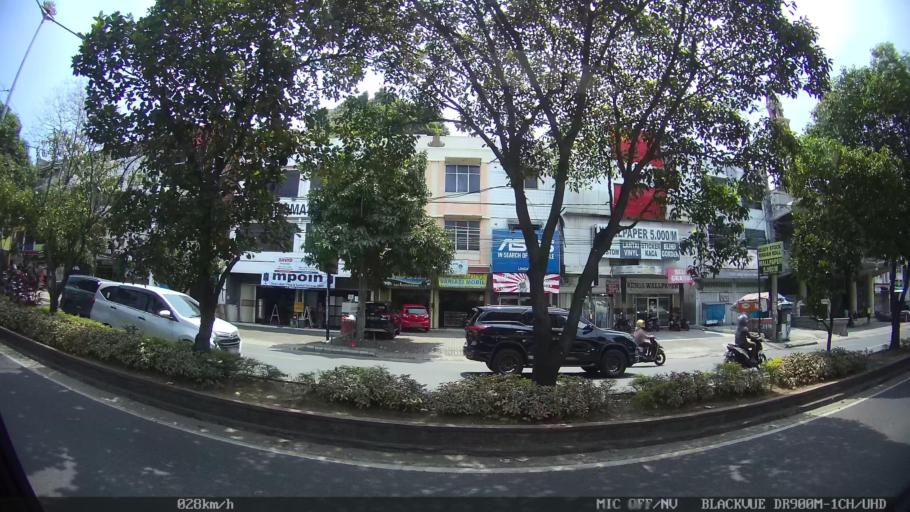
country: ID
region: Lampung
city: Kedaton
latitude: -5.3896
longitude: 105.2620
